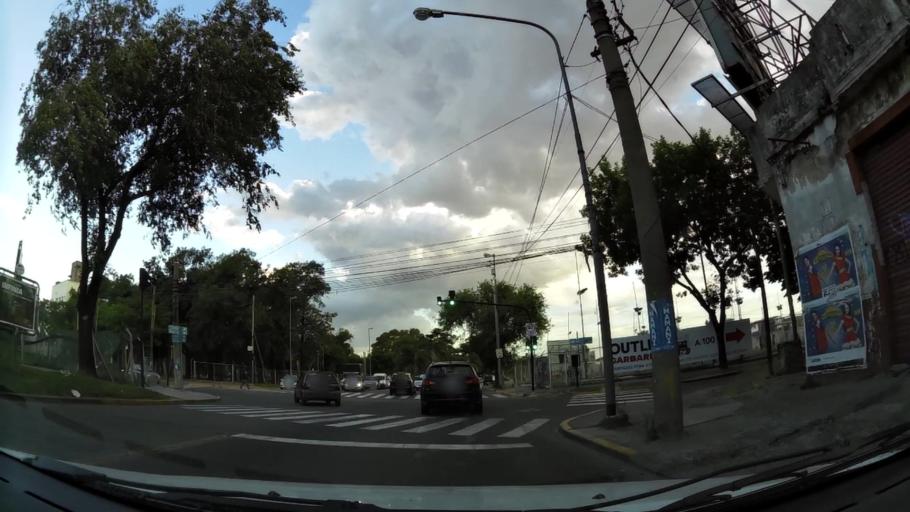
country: AR
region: Buenos Aires
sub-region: Partido de General San Martin
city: General San Martin
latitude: -34.5831
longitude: -58.5193
